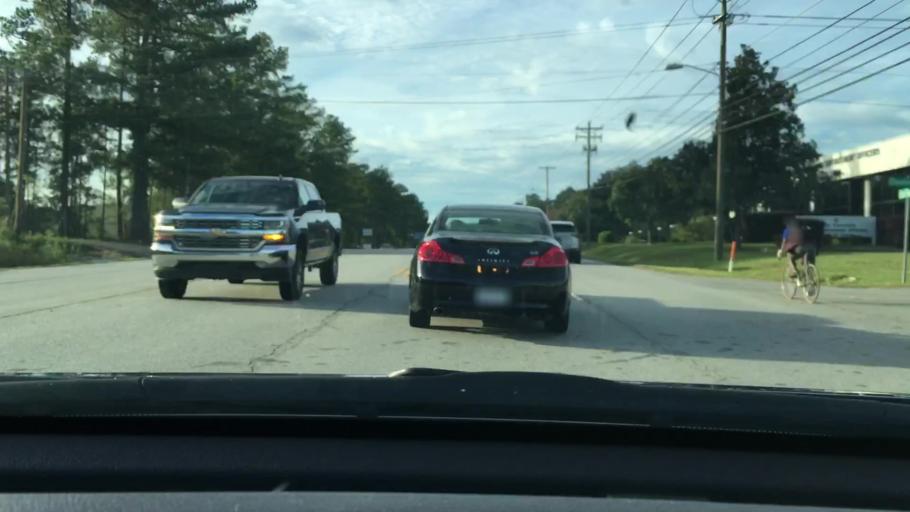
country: US
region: South Carolina
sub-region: Lexington County
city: Saint Andrews
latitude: 34.0760
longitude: -81.1259
